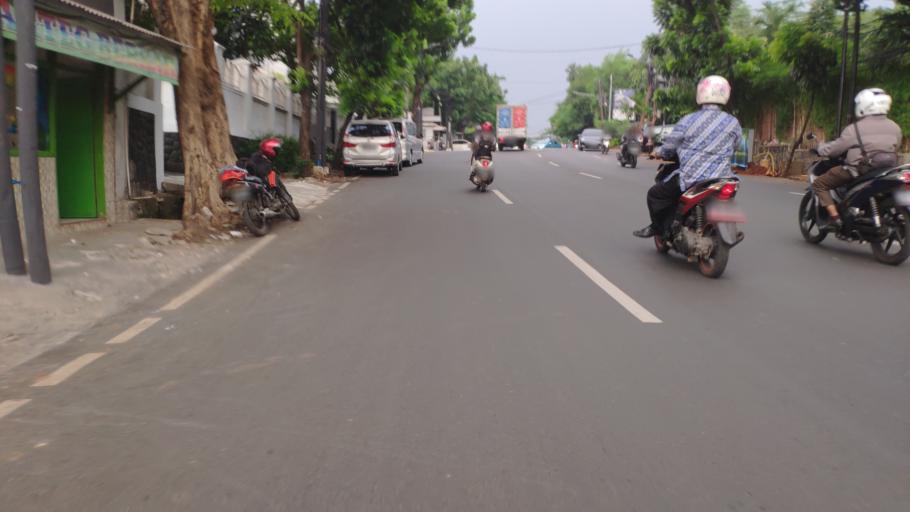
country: ID
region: Jakarta Raya
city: Jakarta
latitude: -6.2774
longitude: 106.8261
